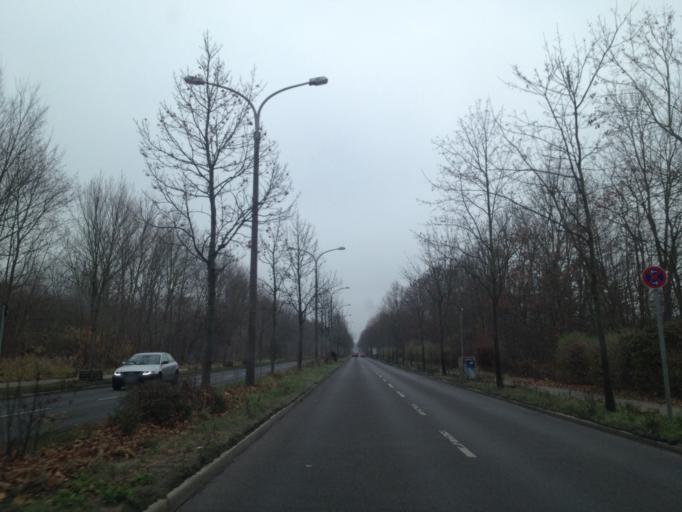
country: DE
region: Berlin
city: Blankenfelde
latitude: 52.6127
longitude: 13.3961
